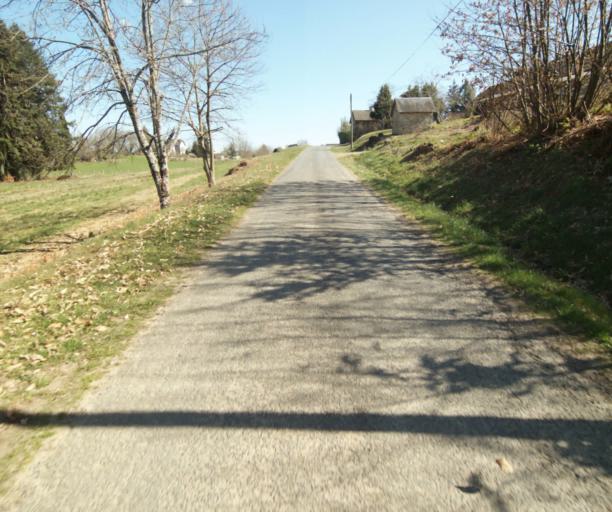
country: FR
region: Limousin
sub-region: Departement de la Correze
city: Saint-Mexant
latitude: 45.2919
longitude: 1.6795
